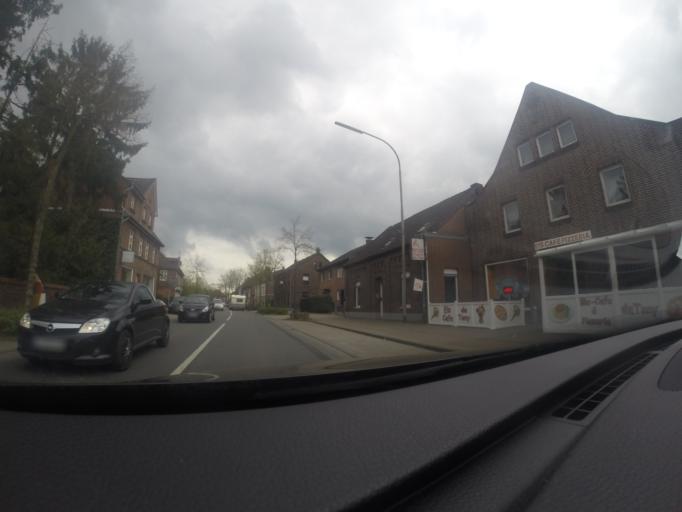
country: DE
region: North Rhine-Westphalia
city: Rees
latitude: 51.6983
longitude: 6.3763
